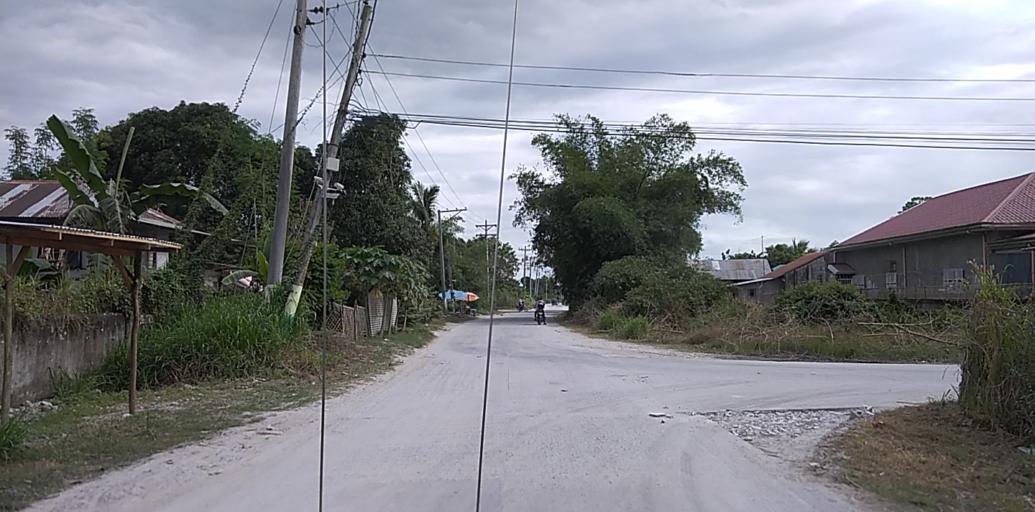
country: PH
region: Central Luzon
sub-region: Province of Pampanga
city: Pulung Santol
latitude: 15.0537
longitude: 120.5608
